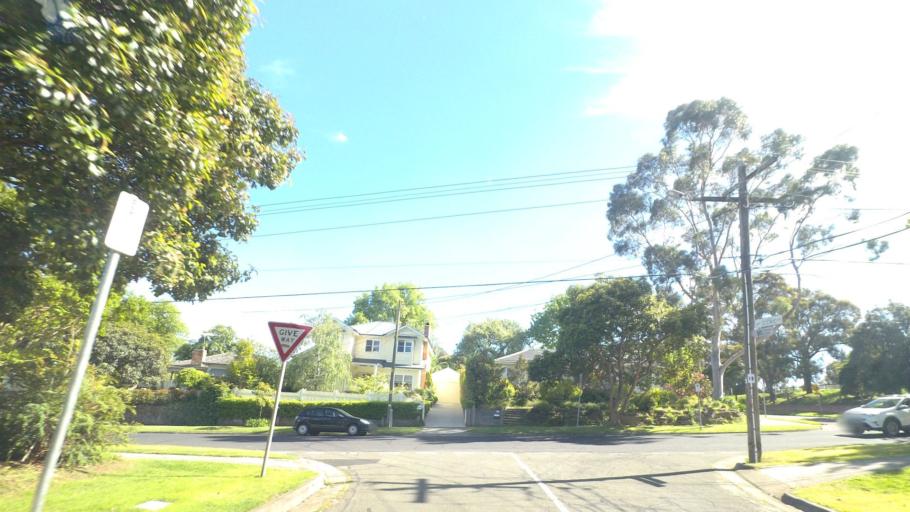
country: AU
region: Victoria
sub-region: Maroondah
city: Ringwood East
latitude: -37.8176
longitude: 145.2511
